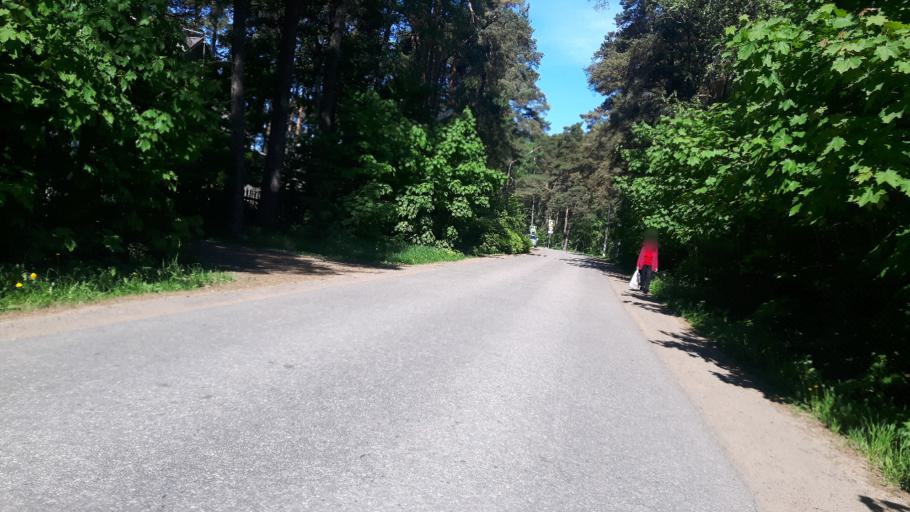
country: RU
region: Leningrad
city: Lebyazh'ye
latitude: 59.9638
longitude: 29.4099
